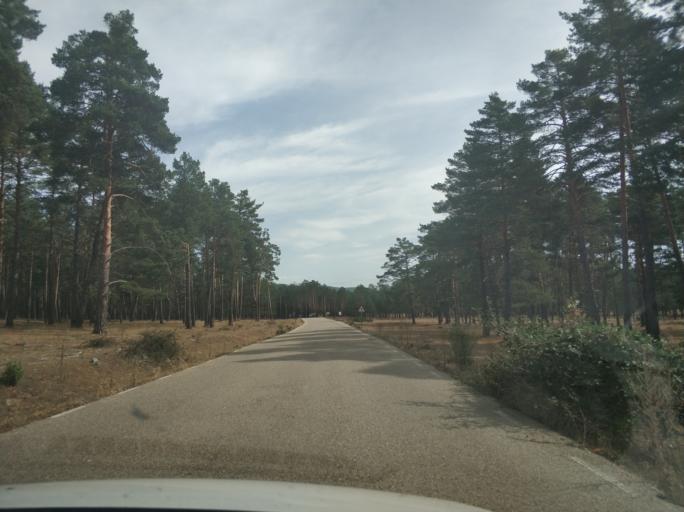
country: ES
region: Castille and Leon
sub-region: Provincia de Soria
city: Navaleno
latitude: 41.8590
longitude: -2.9422
